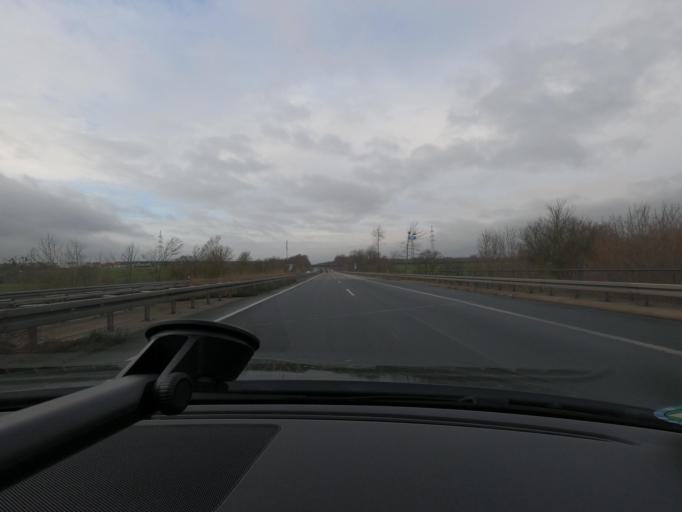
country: DE
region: North Rhine-Westphalia
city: Geseke
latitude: 51.5967
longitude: 8.5238
